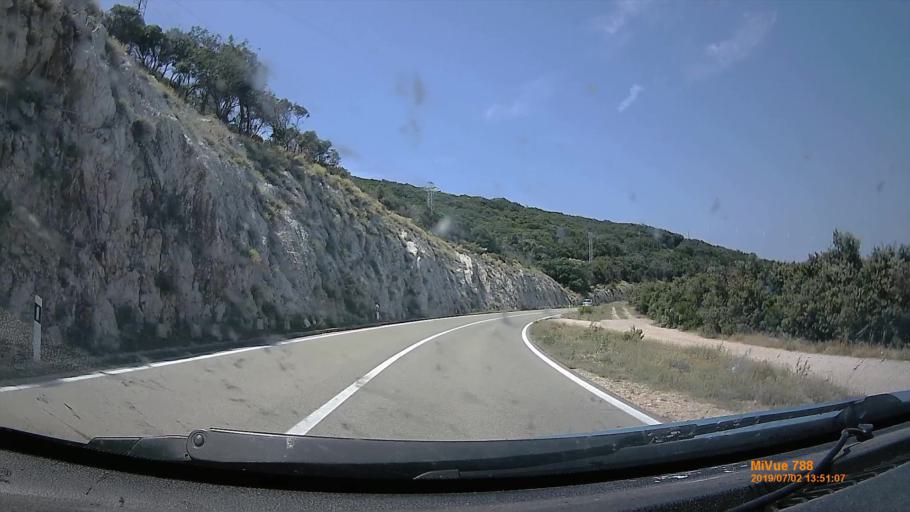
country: HR
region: Primorsko-Goranska
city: Mali Losinj
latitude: 44.6019
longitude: 14.4050
